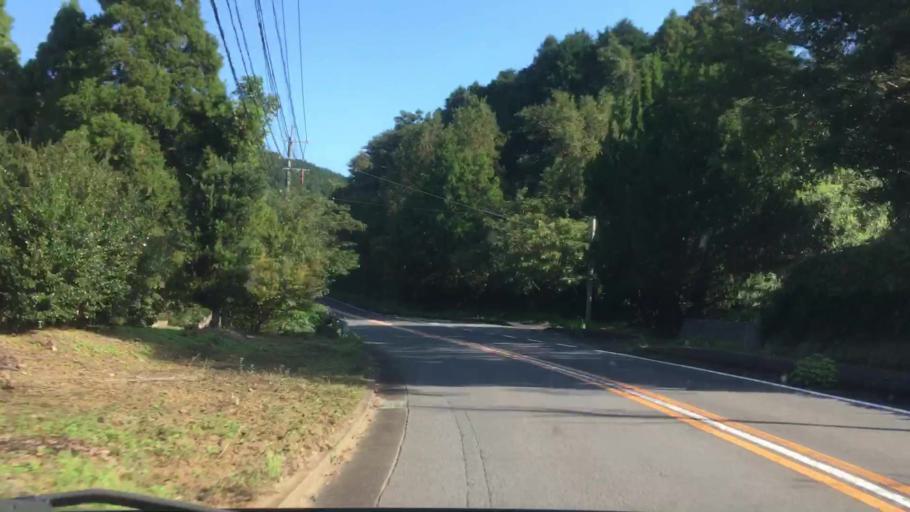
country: JP
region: Nagasaki
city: Sasebo
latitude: 33.0277
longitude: 129.6542
